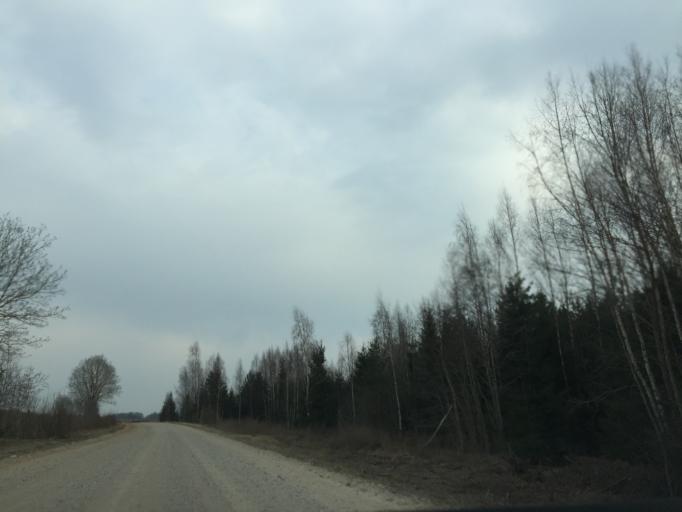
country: LV
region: Priekuli
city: Priekuli
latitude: 57.1911
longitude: 25.4460
